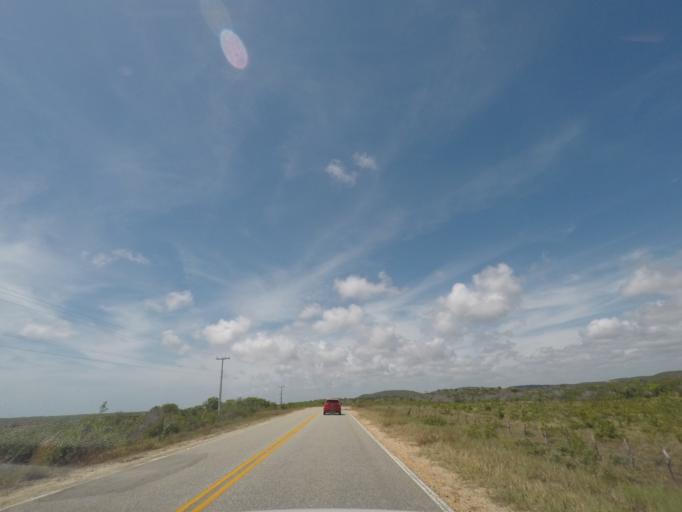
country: BR
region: Sergipe
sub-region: Sao Cristovao
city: Sao Cristovao
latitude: -11.1554
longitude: -37.2020
